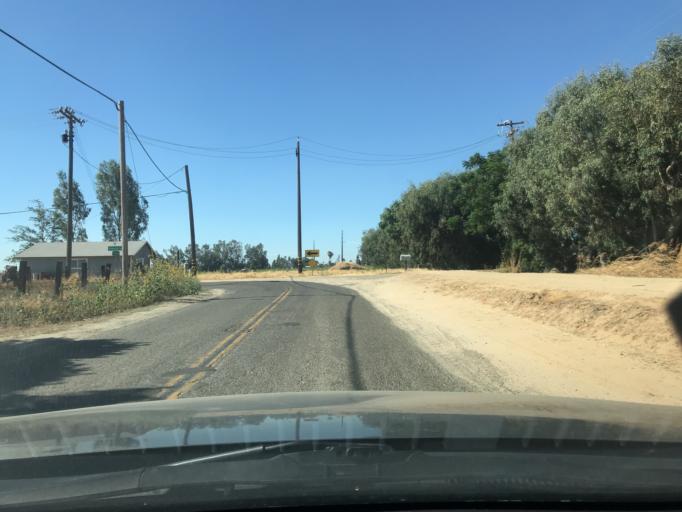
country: US
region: California
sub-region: Merced County
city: Atwater
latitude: 37.3421
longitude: -120.5499
